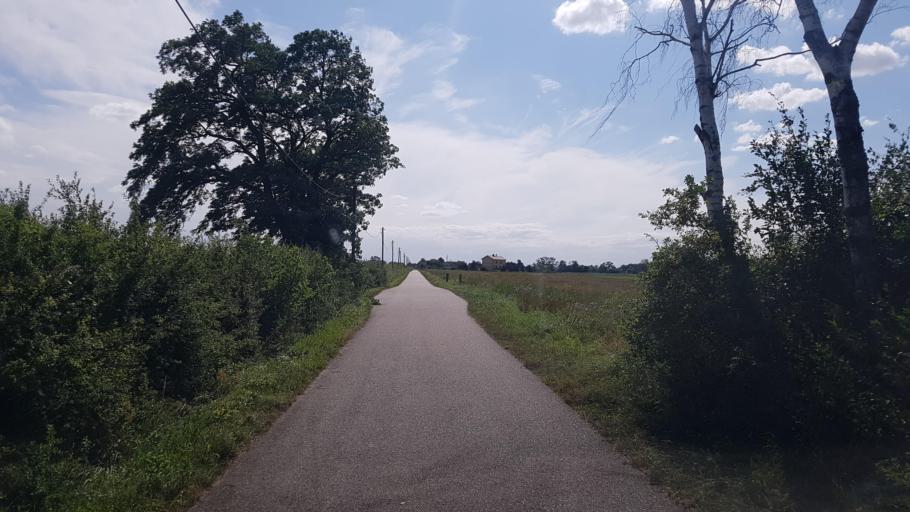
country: DE
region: Brandenburg
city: Muhlberg
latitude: 51.4436
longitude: 13.2897
